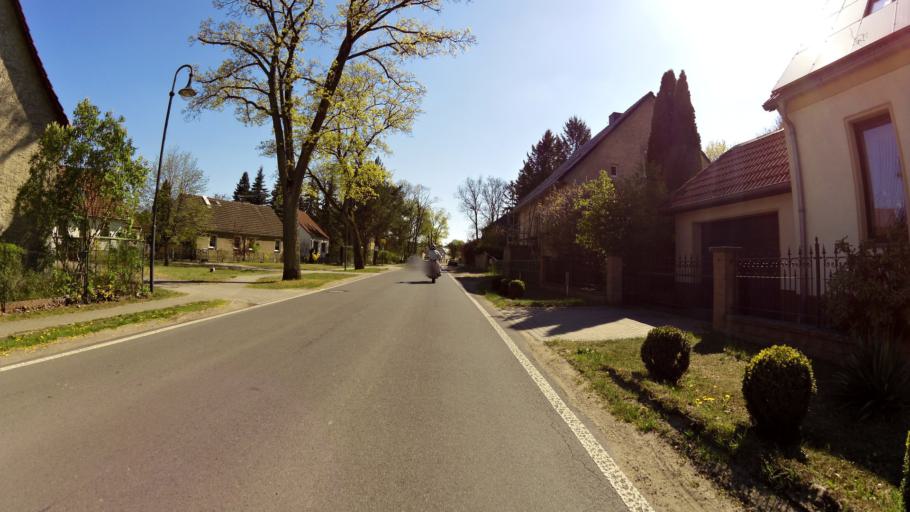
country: DE
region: Brandenburg
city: Rehfelde
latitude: 52.4555
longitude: 13.9562
